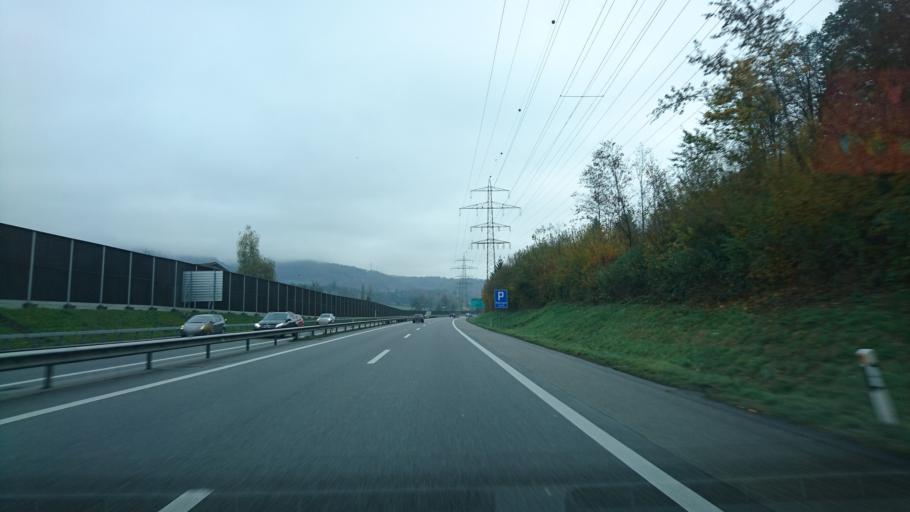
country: CH
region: Aargau
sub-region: Bezirk Zofingen
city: Oftringen
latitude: 47.3125
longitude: 7.9376
